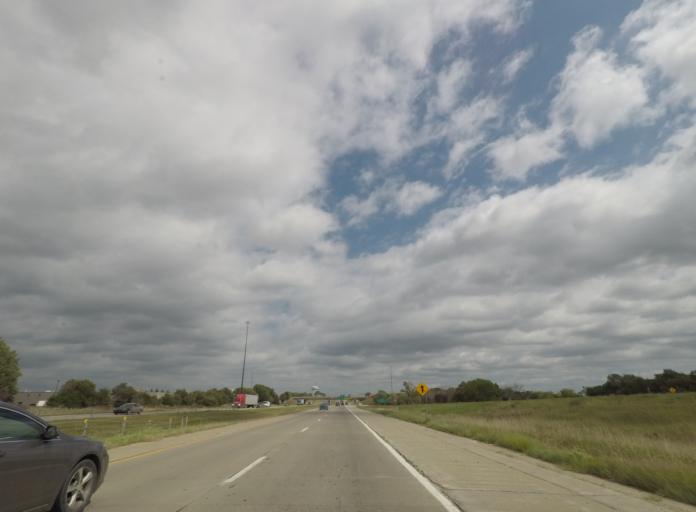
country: US
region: Iowa
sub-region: Linn County
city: Cedar Rapids
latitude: 41.9268
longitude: -91.6620
